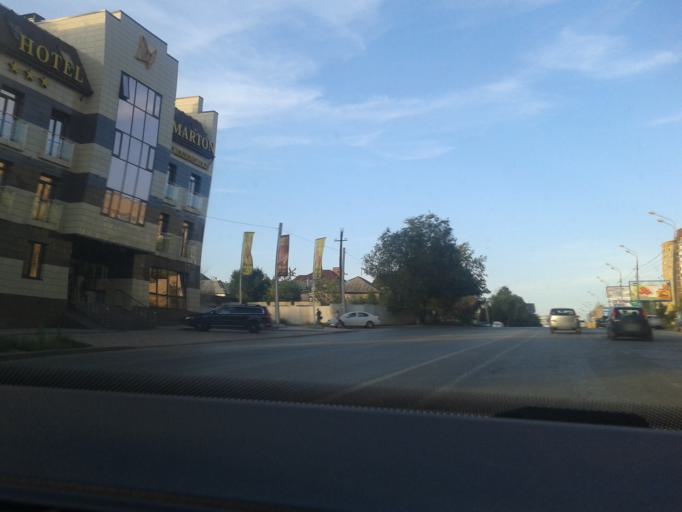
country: RU
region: Volgograd
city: Volgograd
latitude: 48.7198
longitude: 44.5074
